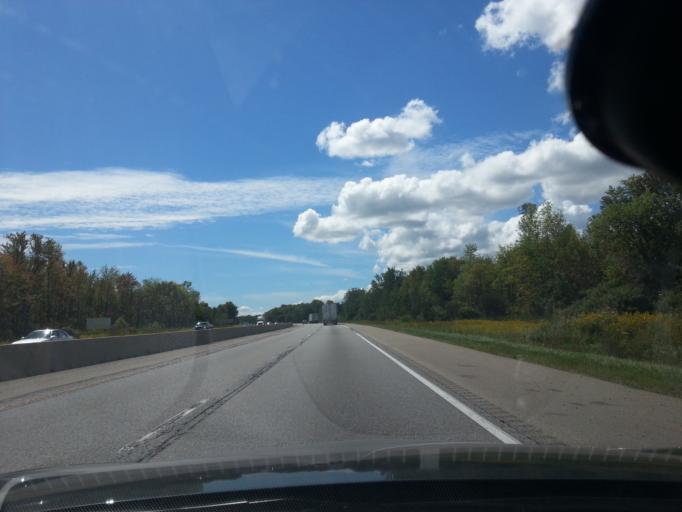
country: CA
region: Ontario
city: Brockville
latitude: 44.6420
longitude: -75.6416
